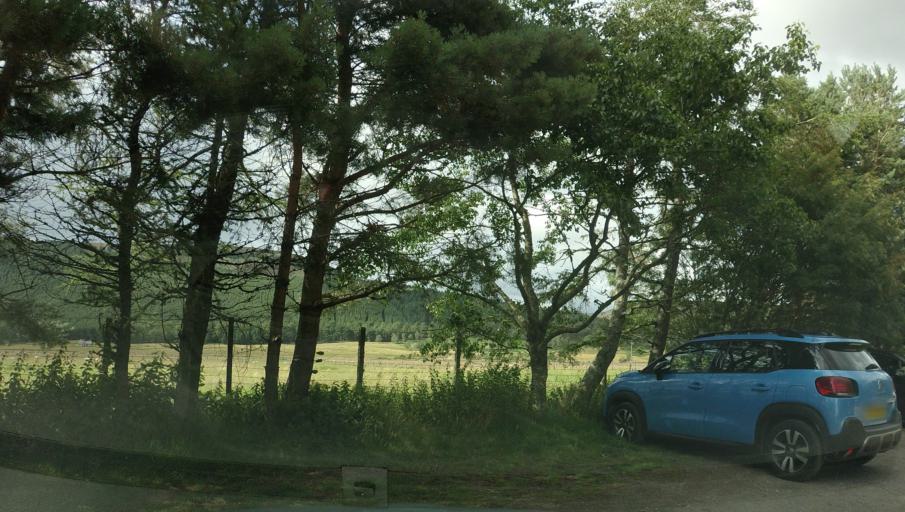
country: GB
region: Scotland
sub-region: Aberdeenshire
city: Ballater
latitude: 57.0135
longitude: -3.3945
